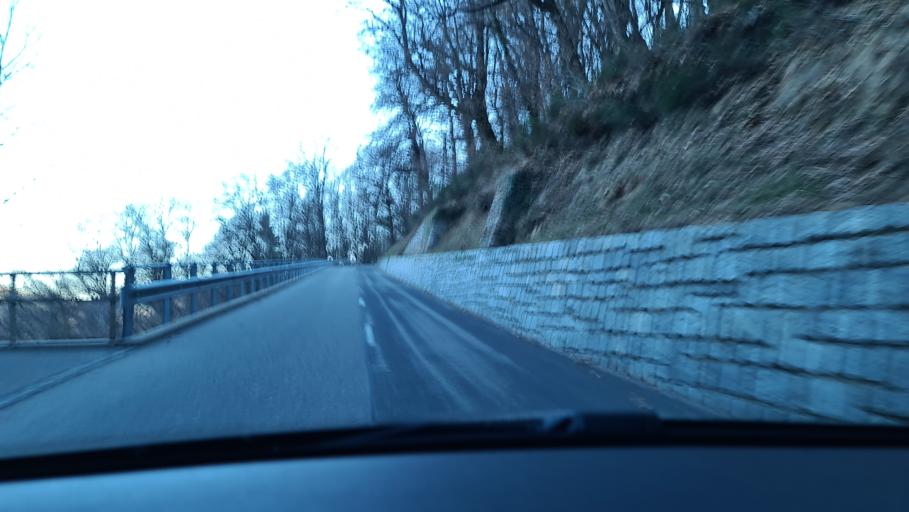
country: CH
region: Ticino
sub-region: Lugano District
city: Gravesano
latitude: 46.0427
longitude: 8.8803
